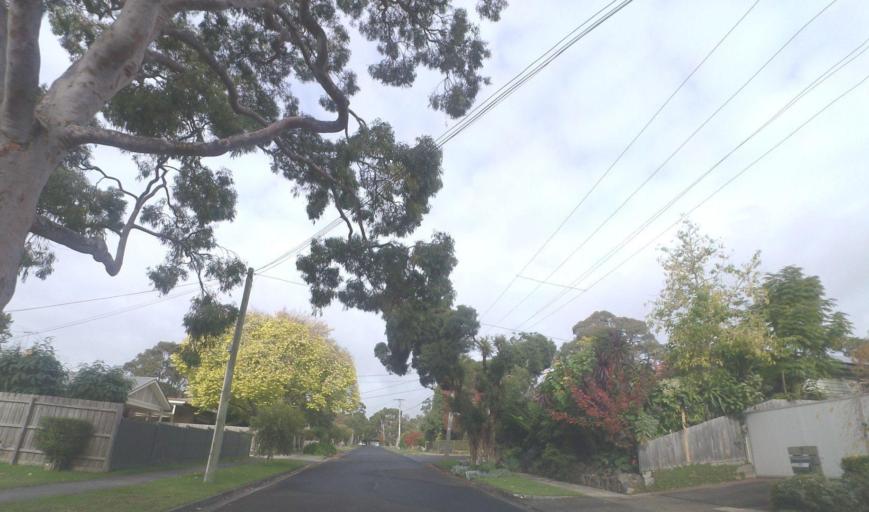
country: AU
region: Victoria
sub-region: Whitehorse
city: Nunawading
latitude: -37.8082
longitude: 145.1715
